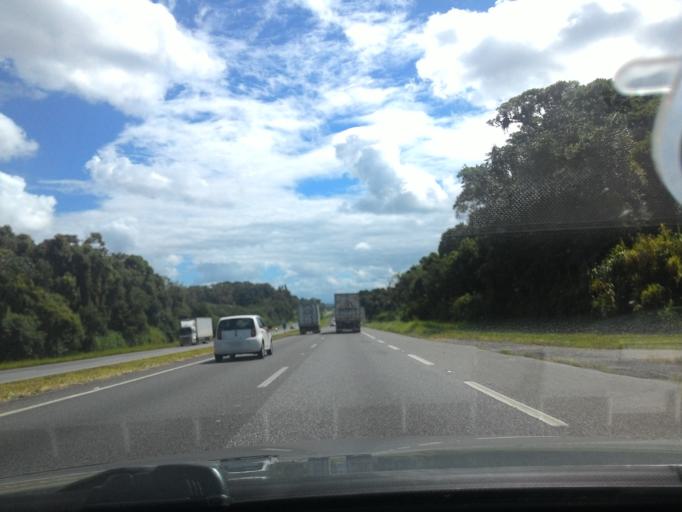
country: BR
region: Sao Paulo
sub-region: Pariquera-Acu
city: Pariquera Acu
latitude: -24.6115
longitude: -47.8842
